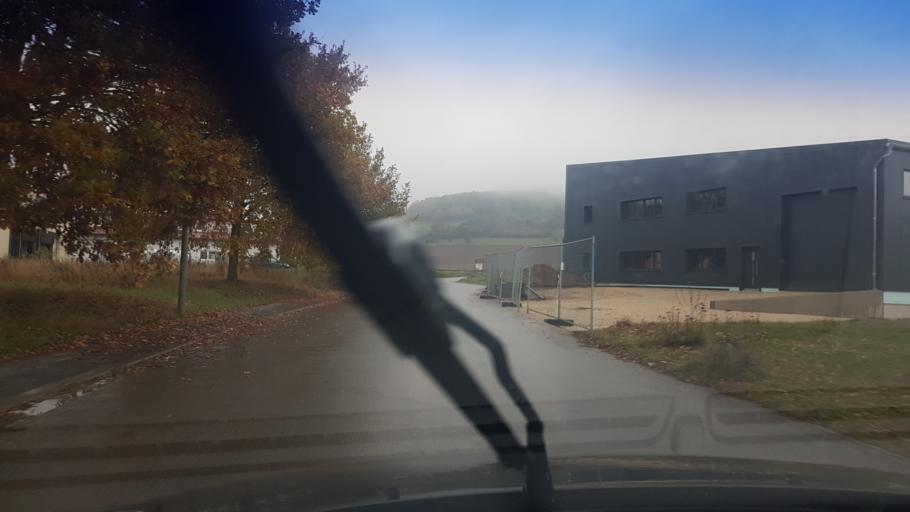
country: DE
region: Bavaria
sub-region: Upper Franconia
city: Baunach
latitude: 49.9936
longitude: 10.8540
